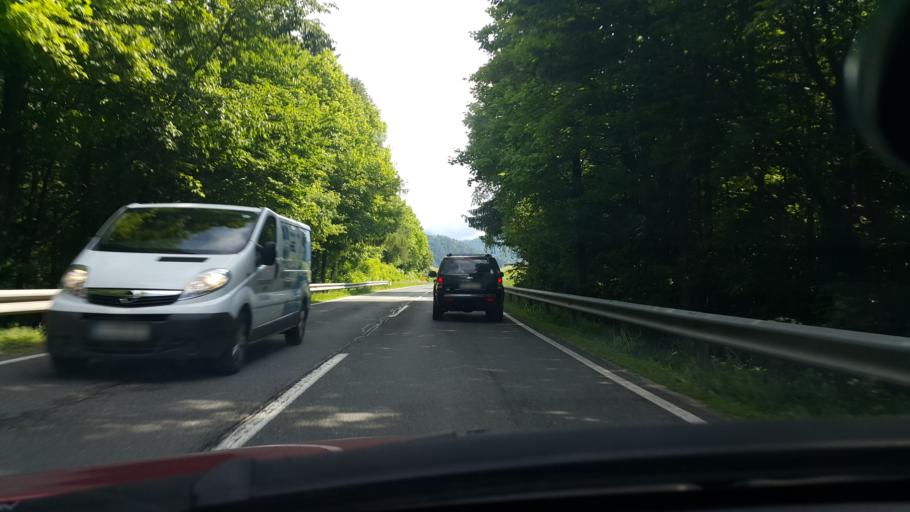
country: SI
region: Trzic
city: Bistrica pri Trzicu
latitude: 46.3491
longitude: 14.2885
